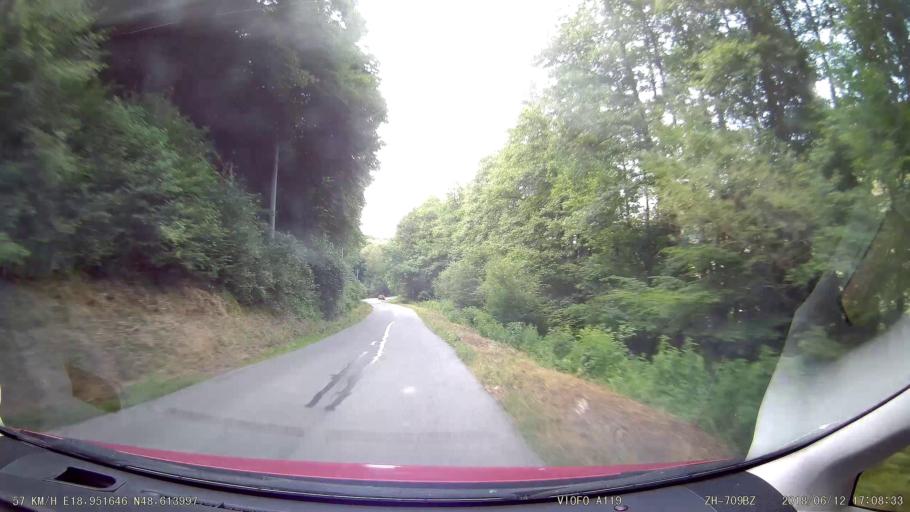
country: SK
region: Banskobystricky
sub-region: Okres Ziar nad Hronom
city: Kremnica
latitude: 48.6141
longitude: 18.9516
